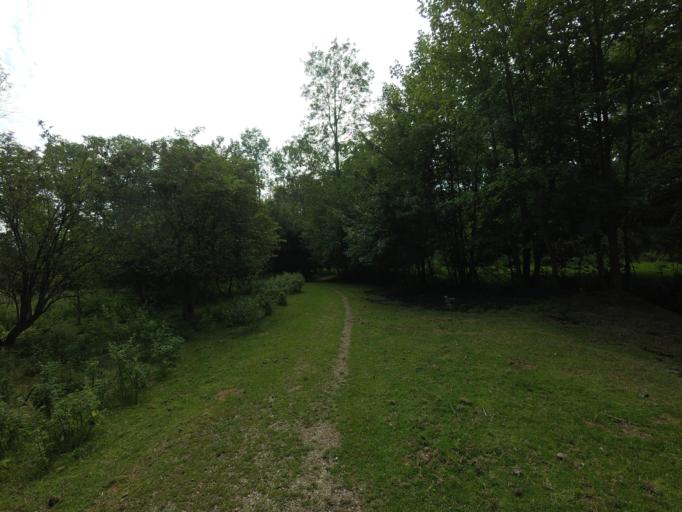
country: NL
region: North Holland
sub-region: Gemeente Huizen
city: Huizen
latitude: 52.3241
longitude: 5.2889
